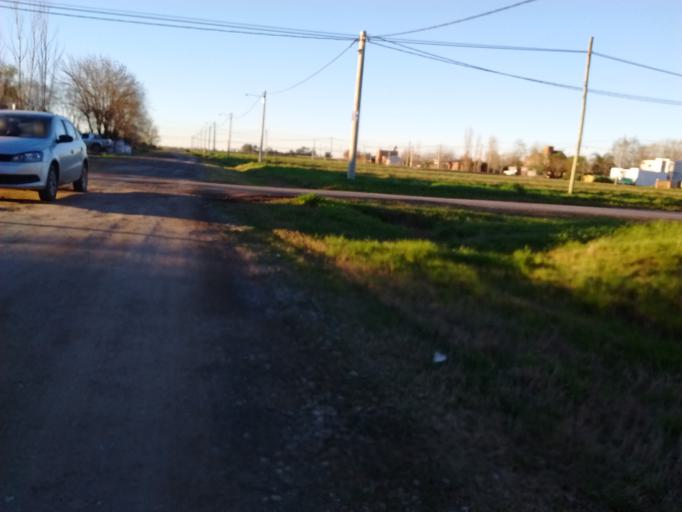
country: AR
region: Santa Fe
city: Funes
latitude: -32.9130
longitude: -60.8516
